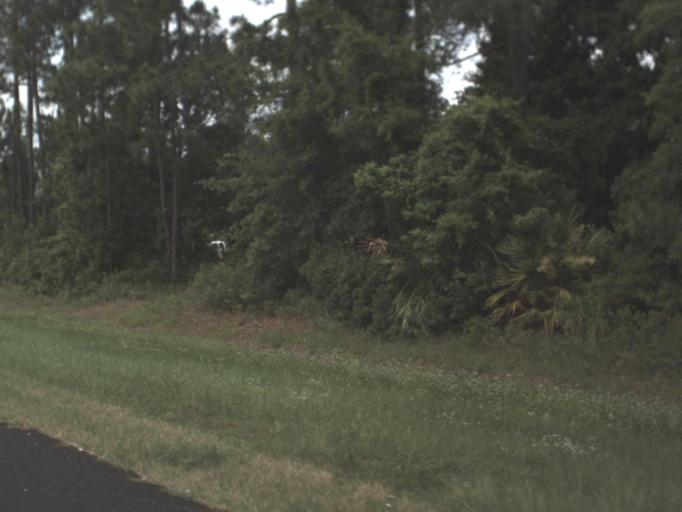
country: US
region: Florida
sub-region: Saint Johns County
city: Fruit Cove
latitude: 30.0874
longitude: -81.7065
